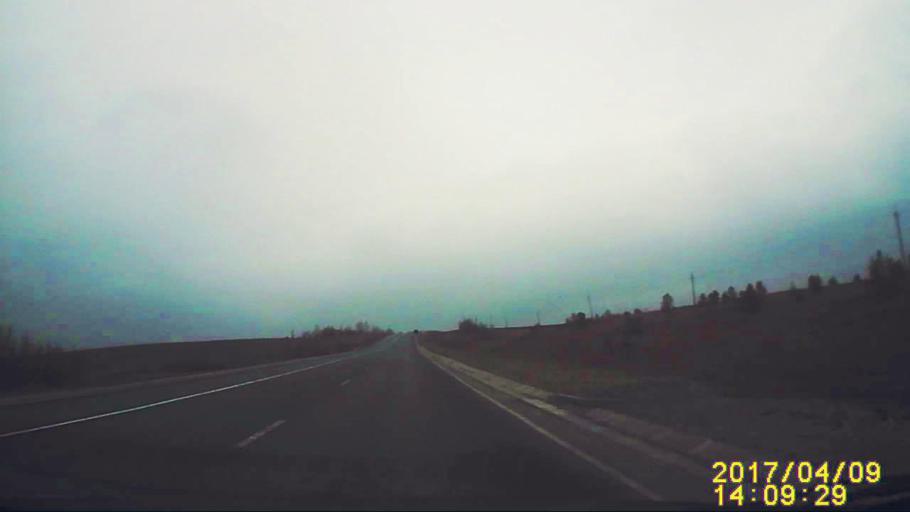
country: RU
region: Ulyanovsk
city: Krasnyy Gulyay
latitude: 54.0292
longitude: 48.2131
